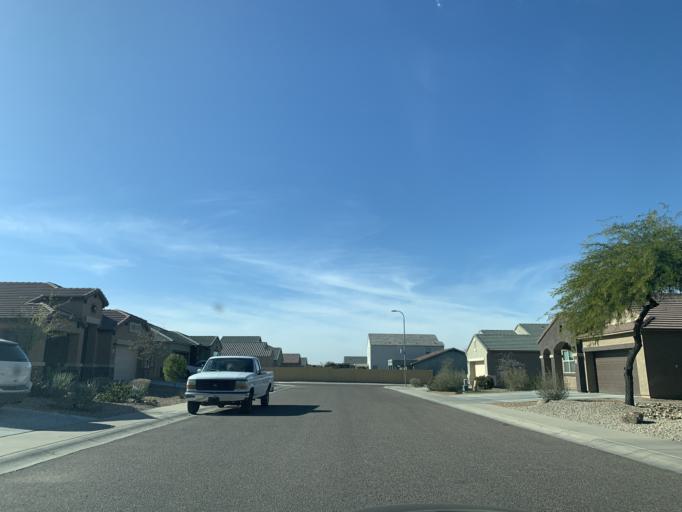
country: US
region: Arizona
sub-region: Maricopa County
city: Laveen
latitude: 33.3939
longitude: -112.1209
